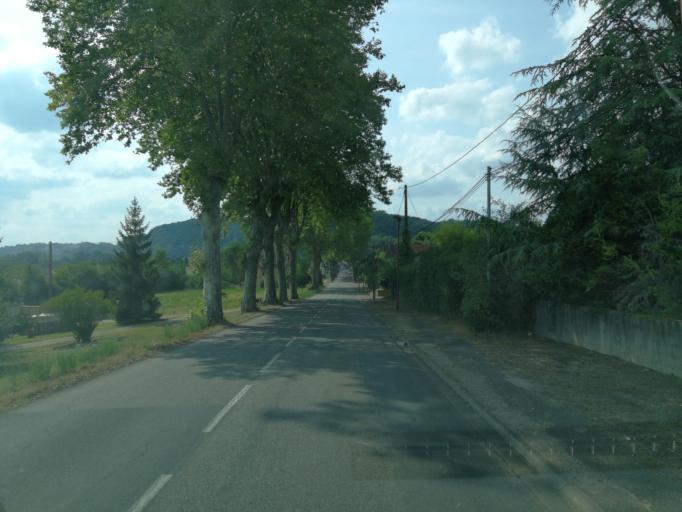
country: FR
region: Aquitaine
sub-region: Departement du Lot-et-Garonne
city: Montayral
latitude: 44.4953
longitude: 0.9937
